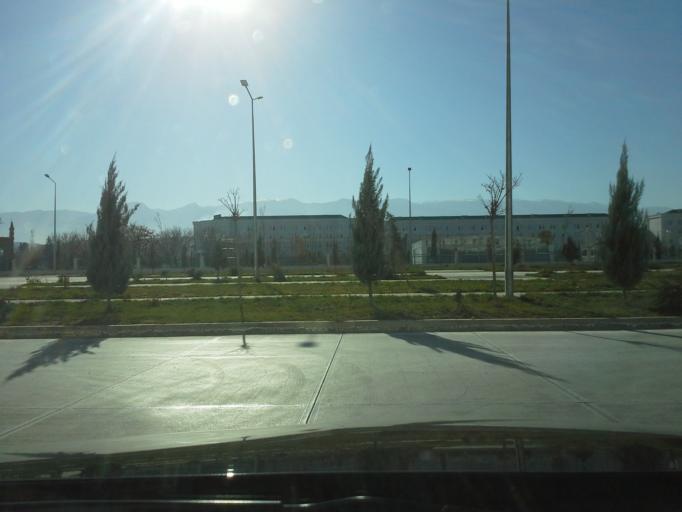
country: TM
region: Ahal
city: Ashgabat
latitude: 37.9675
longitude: 58.3353
